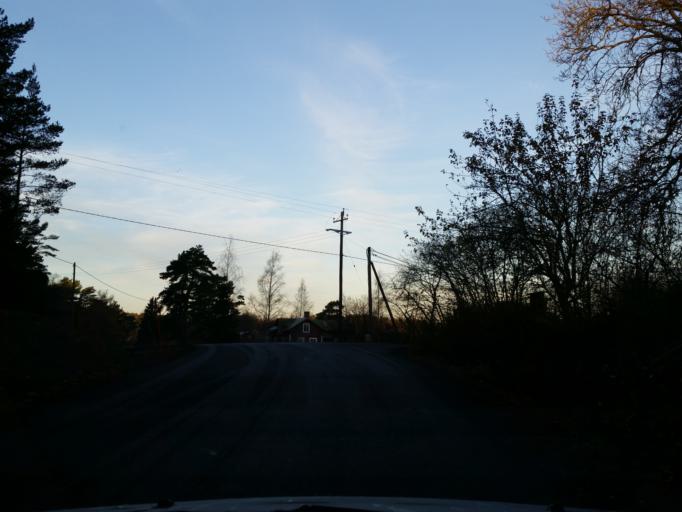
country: AX
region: Alands landsbygd
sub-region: Sund
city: Sund
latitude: 60.2299
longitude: 20.0894
